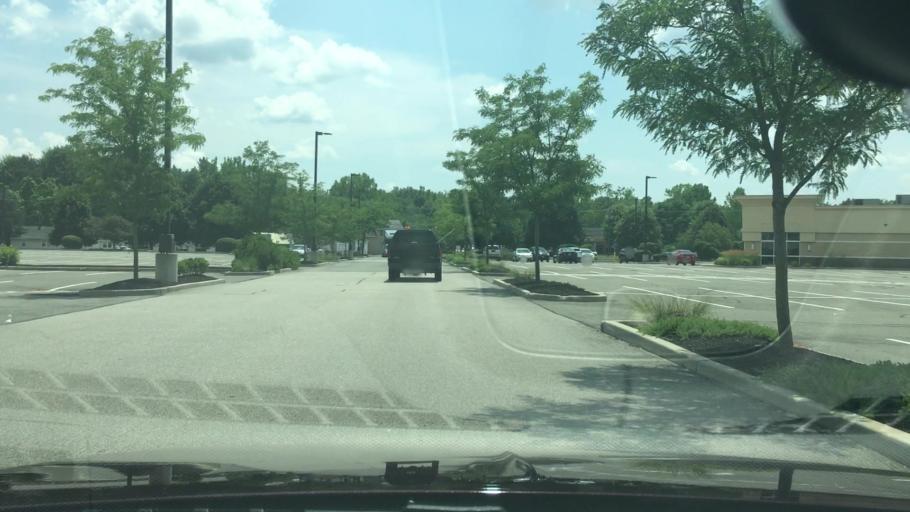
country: US
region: Connecticut
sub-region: Hartford County
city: Kensington
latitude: 41.6434
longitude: -72.7300
